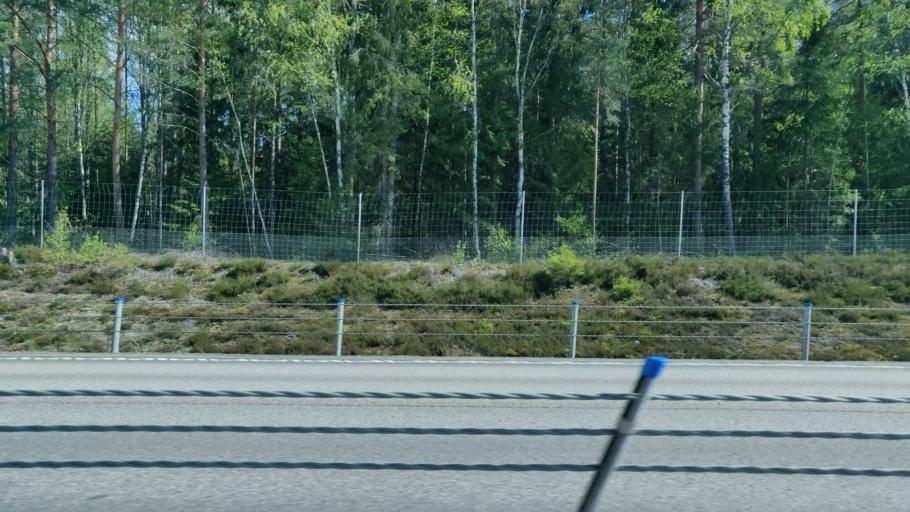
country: SE
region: Vaermland
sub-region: Karlstads Kommun
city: Karlstad
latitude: 59.4229
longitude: 13.5337
